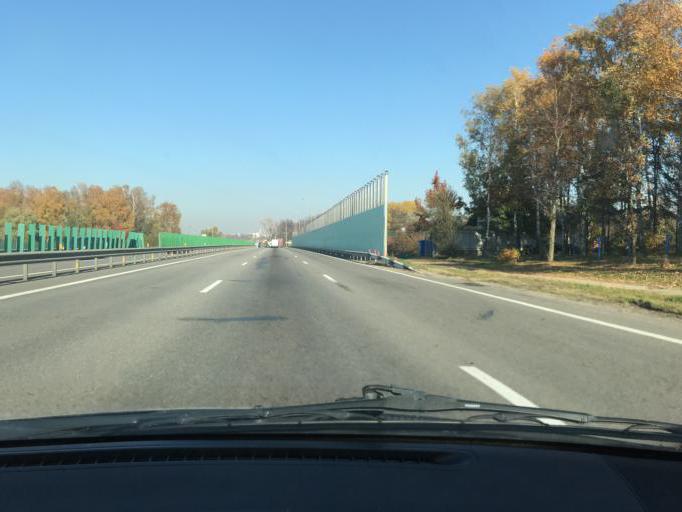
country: BY
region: Minsk
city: Syenitsa
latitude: 53.8218
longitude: 27.5324
